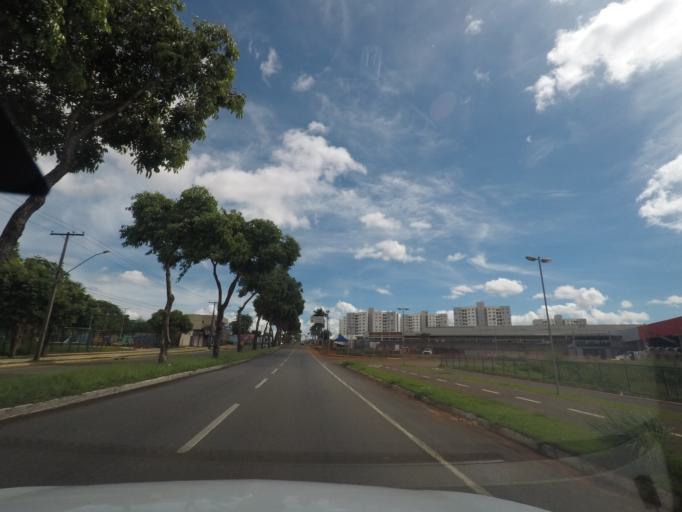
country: BR
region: Goias
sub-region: Goiania
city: Goiania
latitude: -16.7300
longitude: -49.3247
